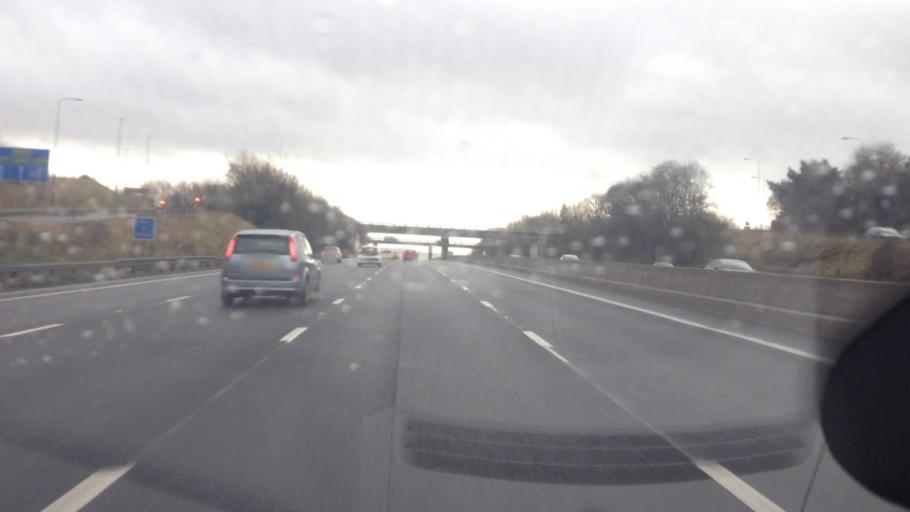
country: GB
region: England
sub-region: City and Borough of Wakefield
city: Ossett
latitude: 53.6860
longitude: -1.5556
